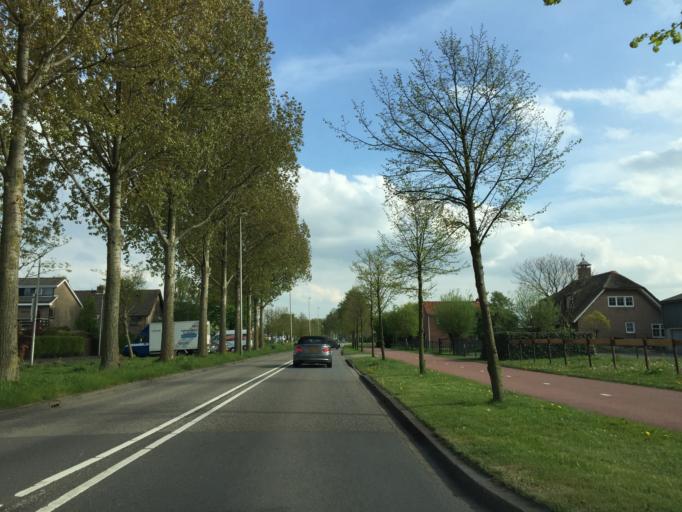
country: NL
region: South Holland
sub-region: Gemeente Pijnacker-Nootdorp
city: Pijnacker
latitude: 52.0172
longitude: 4.4289
